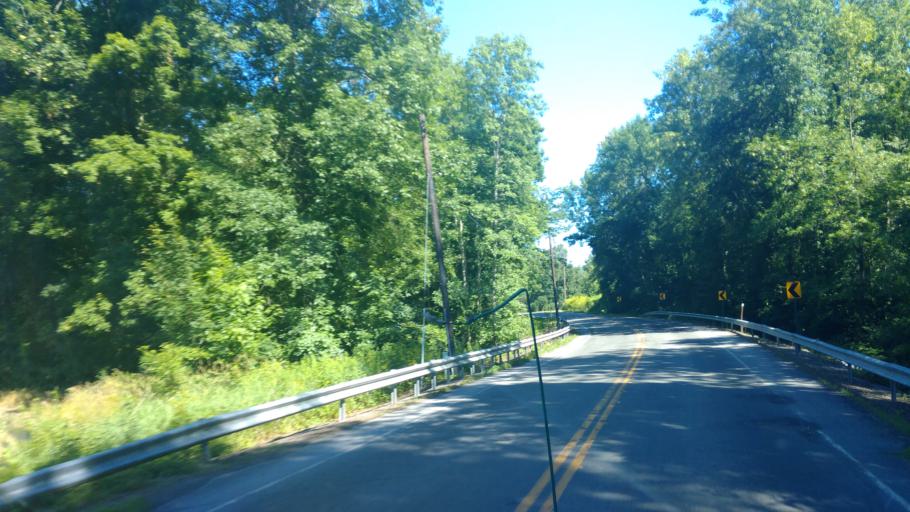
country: US
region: New York
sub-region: Wayne County
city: Lyons
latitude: 43.0231
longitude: -76.9420
